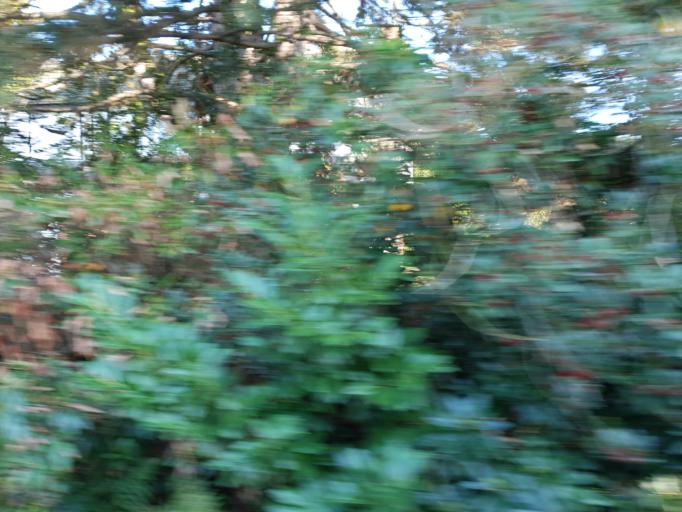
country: BE
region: Flanders
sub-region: Provincie Antwerpen
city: Boechout
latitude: 51.1526
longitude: 4.5210
